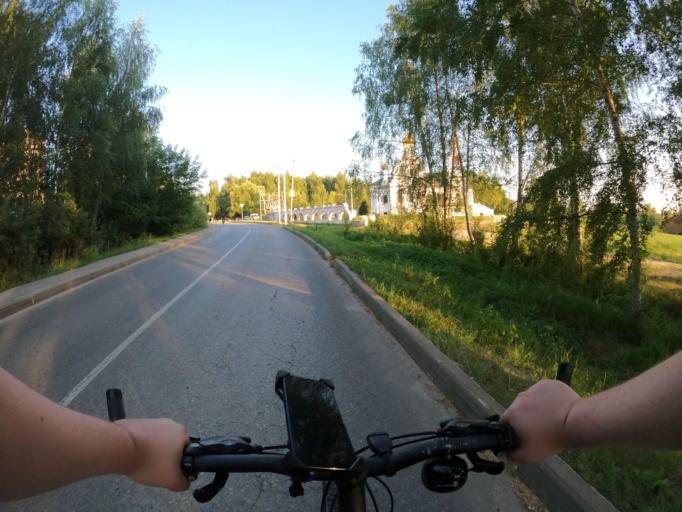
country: RU
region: Moskovskaya
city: Beloozerskiy
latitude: 55.4623
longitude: 38.4321
